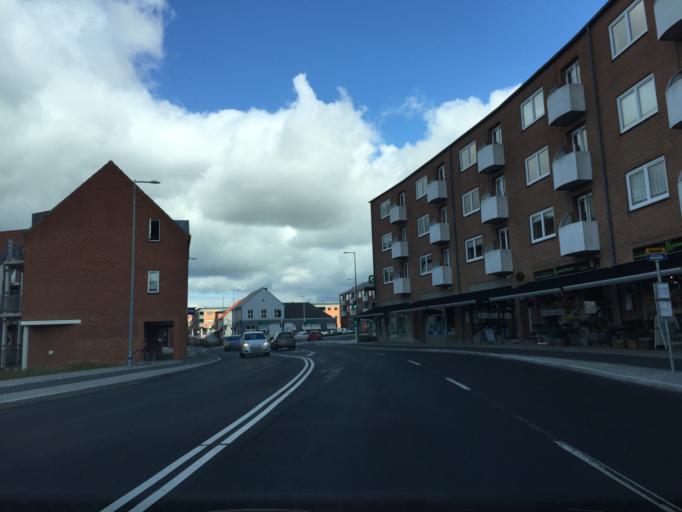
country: DK
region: Central Jutland
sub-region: Silkeborg Kommune
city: Silkeborg
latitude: 56.1768
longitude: 9.5547
